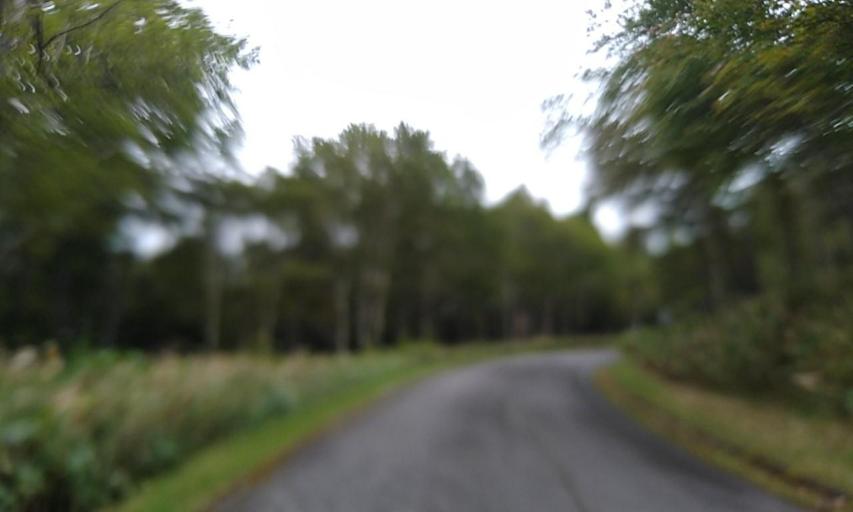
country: JP
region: Hokkaido
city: Bihoro
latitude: 43.5672
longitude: 144.2181
